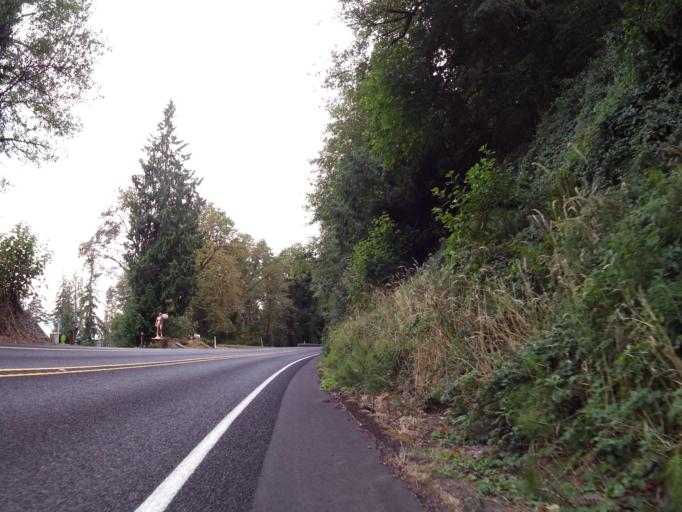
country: US
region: Oregon
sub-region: Columbia County
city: Clatskanie
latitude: 46.1707
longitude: -123.2347
